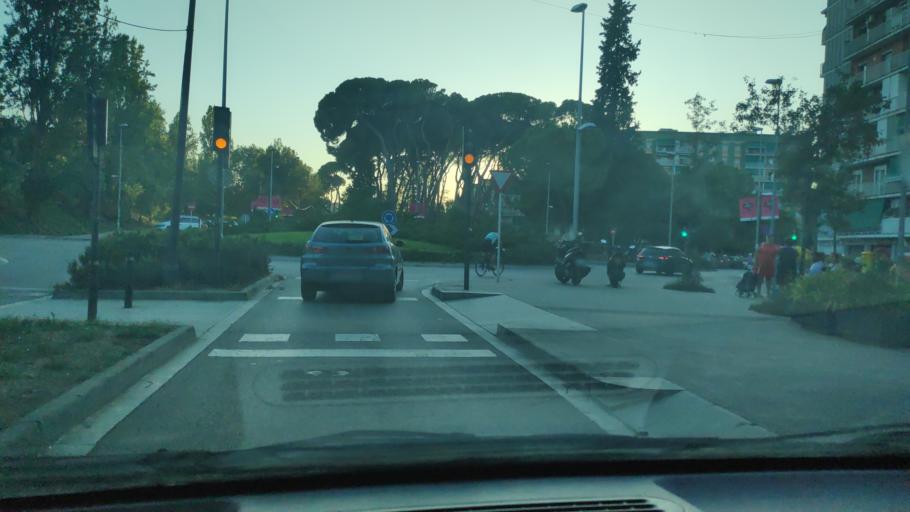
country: ES
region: Catalonia
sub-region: Provincia de Barcelona
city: Cerdanyola del Valles
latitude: 41.4892
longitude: 2.1483
